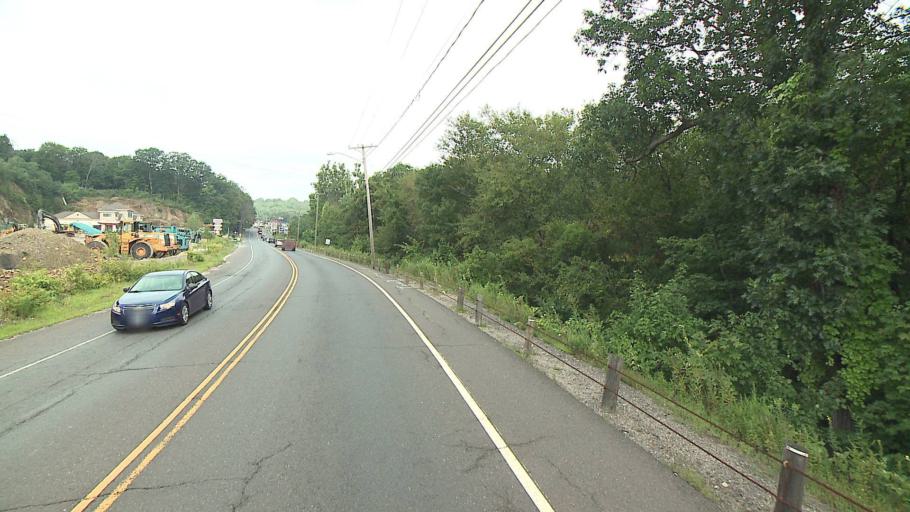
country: US
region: Connecticut
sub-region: Litchfield County
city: Oakville
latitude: 41.5825
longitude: -73.0727
